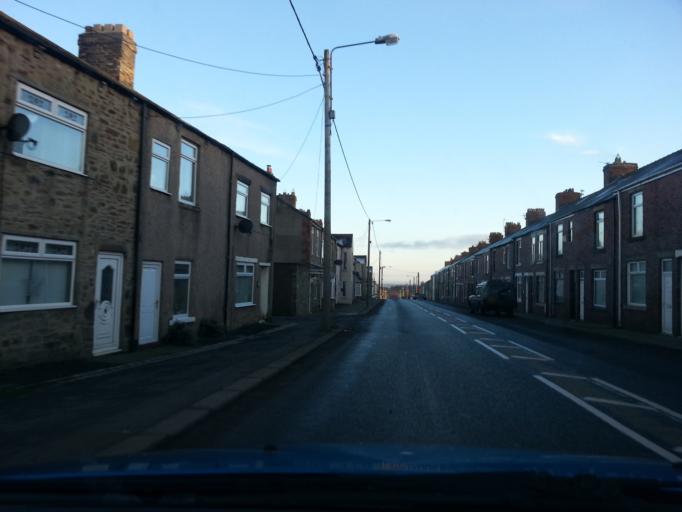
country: GB
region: England
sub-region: County Durham
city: Crook
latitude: 54.7335
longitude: -1.7431
